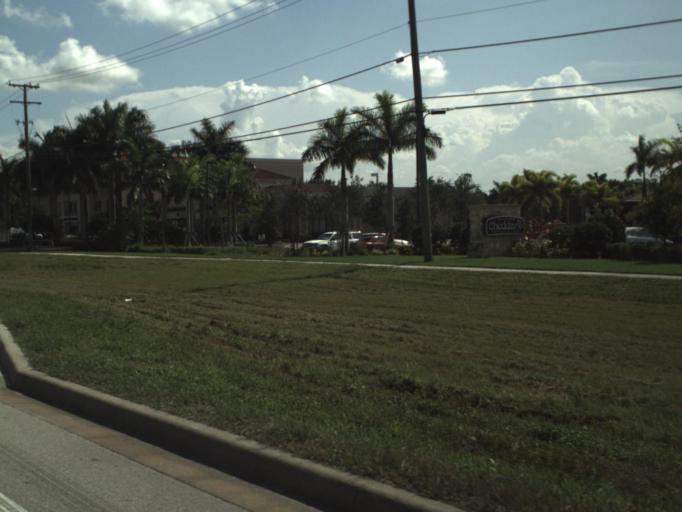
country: US
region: Florida
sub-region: Palm Beach County
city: Wellington
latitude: 26.6643
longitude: -80.2031
